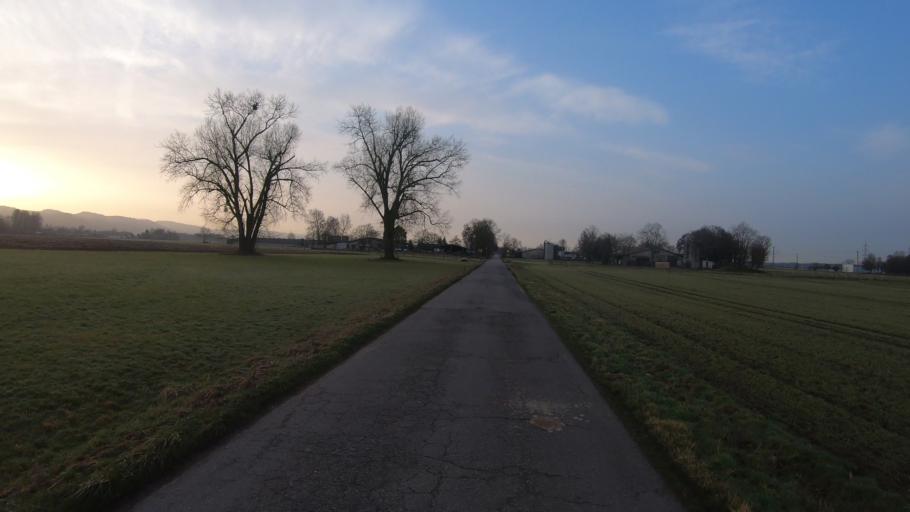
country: DE
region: Baden-Wuerttemberg
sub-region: Karlsruhe Region
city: Hemsbach
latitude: 49.6055
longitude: 8.6167
